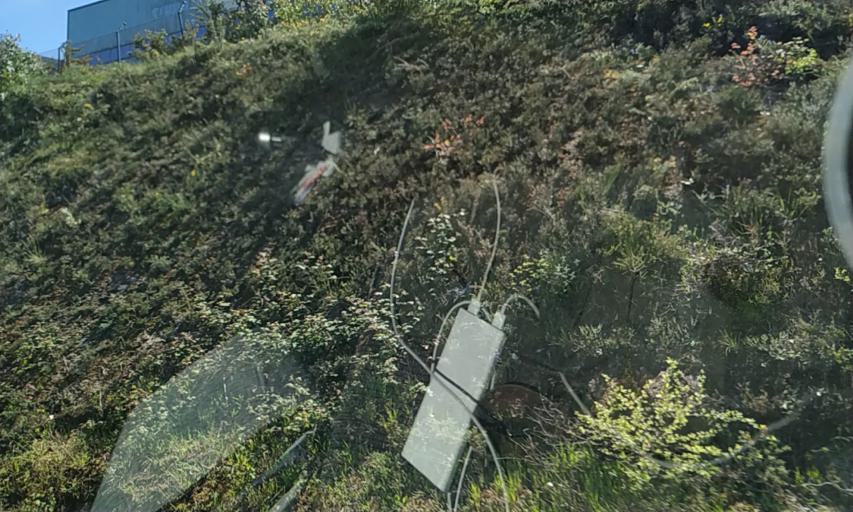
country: ES
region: Galicia
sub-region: Provincia da Coruna
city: Santiago de Compostela
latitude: 42.9074
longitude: -8.5107
